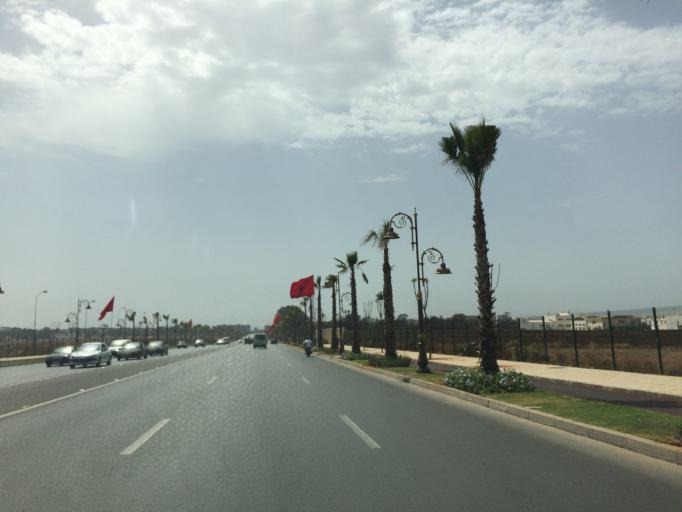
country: MA
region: Rabat-Sale-Zemmour-Zaer
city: Sale
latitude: 34.0320
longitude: -6.7640
